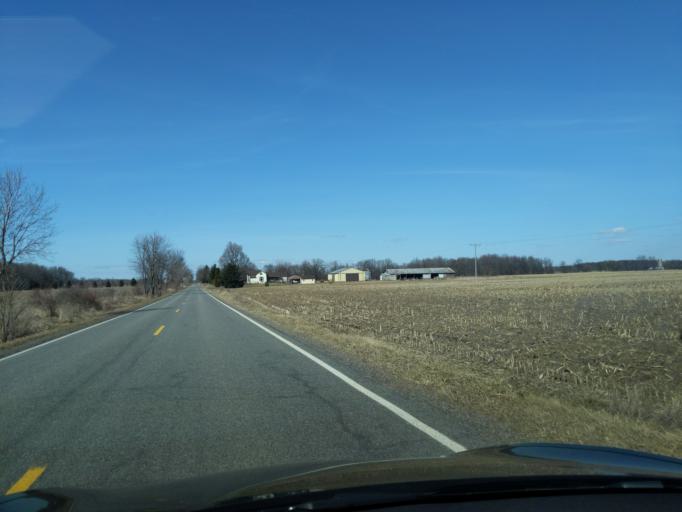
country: US
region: Michigan
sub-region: Ionia County
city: Saranac
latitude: 42.9174
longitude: -85.1341
